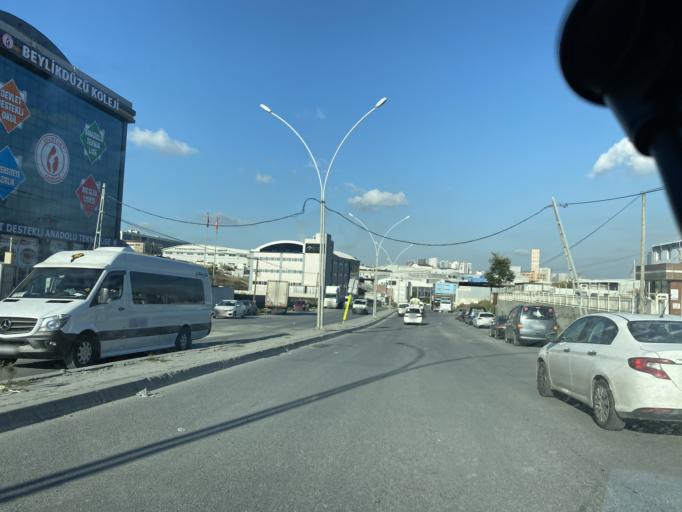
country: TR
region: Istanbul
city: Esenyurt
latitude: 41.0489
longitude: 28.6447
